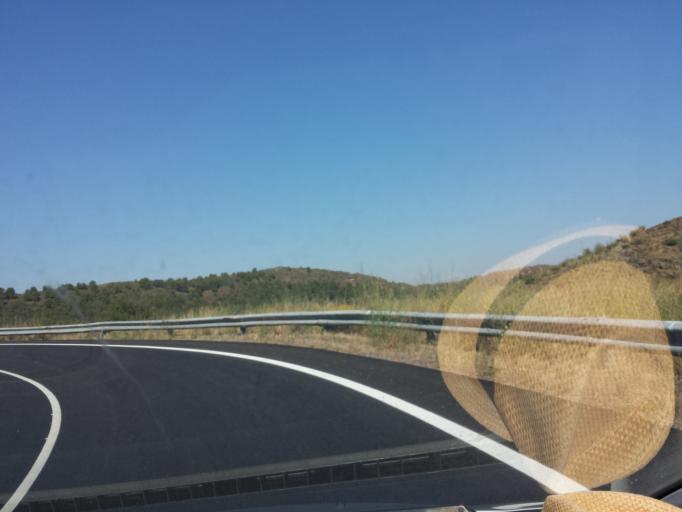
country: ES
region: Aragon
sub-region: Provincia de Zaragoza
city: Nuevalos
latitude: 41.2154
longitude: -1.7604
